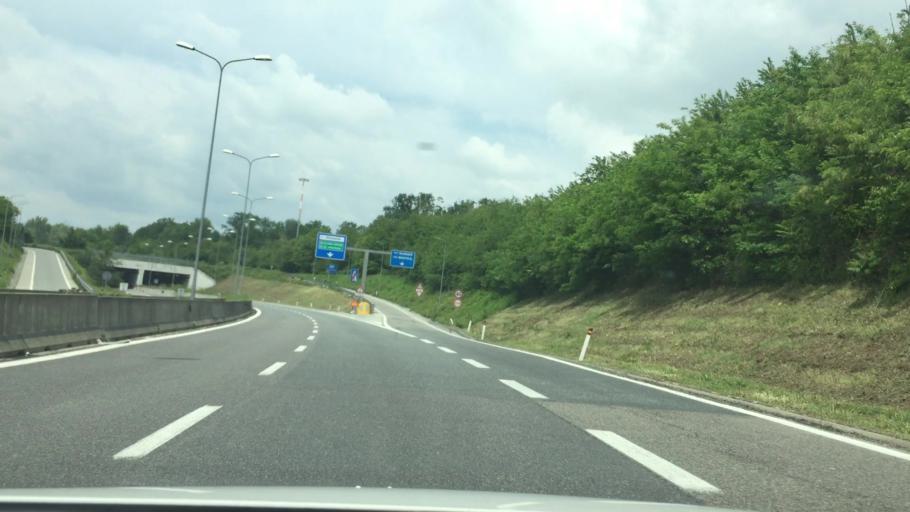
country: IT
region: Lombardy
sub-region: Provincia di Varese
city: Lonate Pozzolo
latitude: 45.5823
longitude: 8.7281
